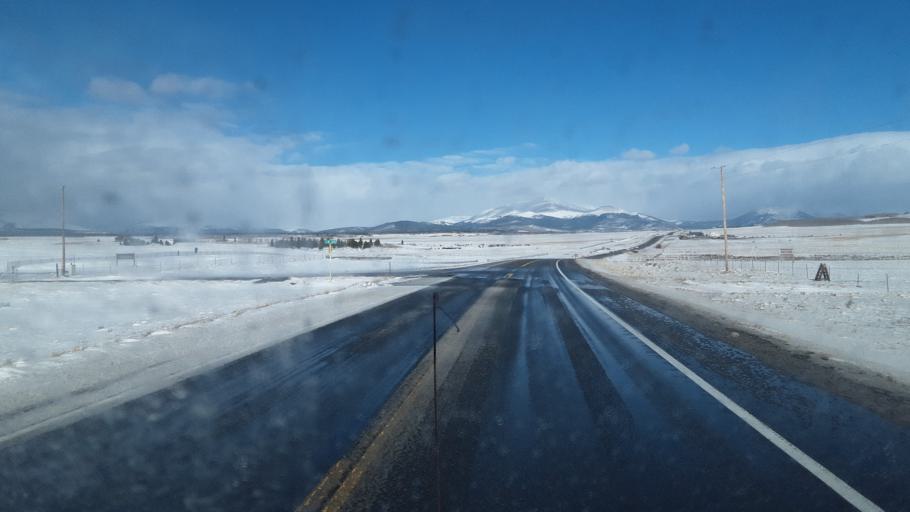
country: US
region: Colorado
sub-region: Park County
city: Fairplay
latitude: 39.1677
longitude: -106.0018
